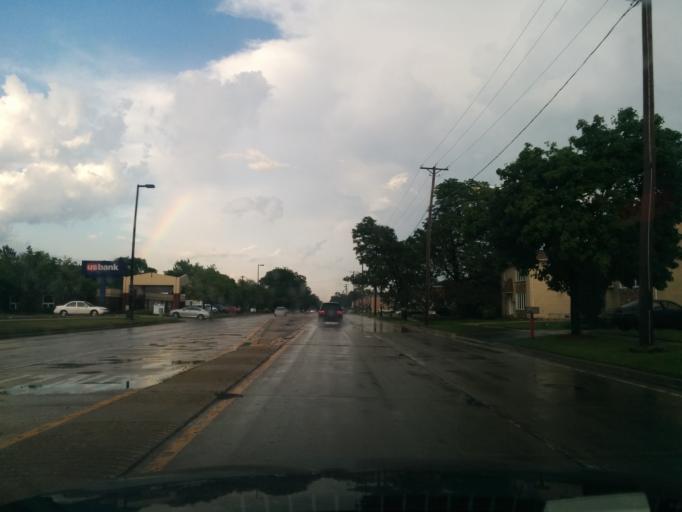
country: US
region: Illinois
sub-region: Cook County
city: Burbank
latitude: 41.7342
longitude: -87.7576
